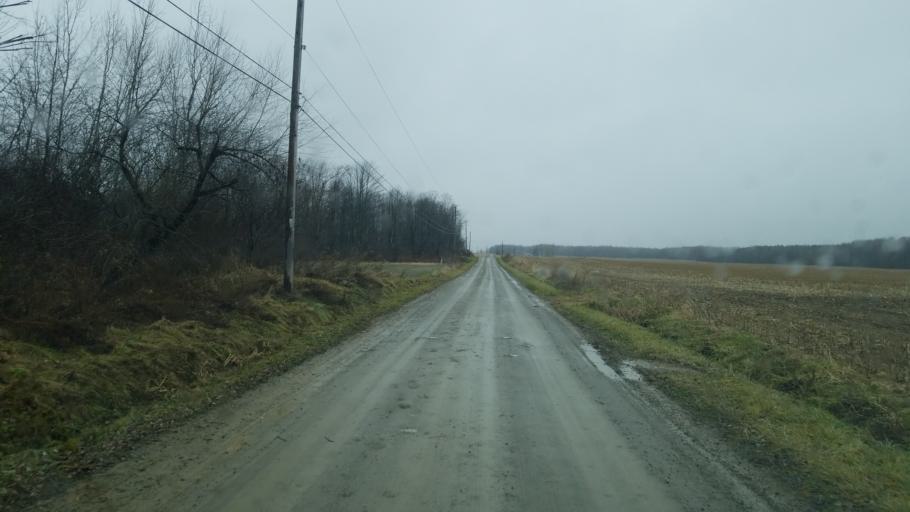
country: US
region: Ohio
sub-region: Ashtabula County
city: Roaming Shores
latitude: 41.5804
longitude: -80.7055
